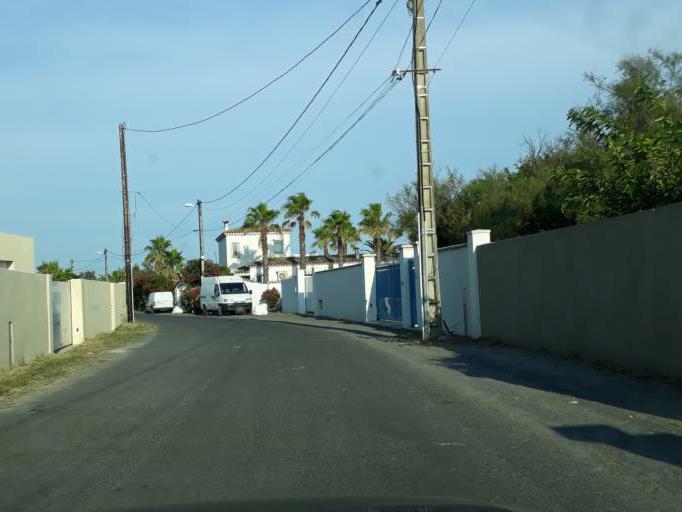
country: FR
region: Languedoc-Roussillon
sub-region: Departement de l'Herault
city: Agde
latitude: 43.2773
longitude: 3.4683
